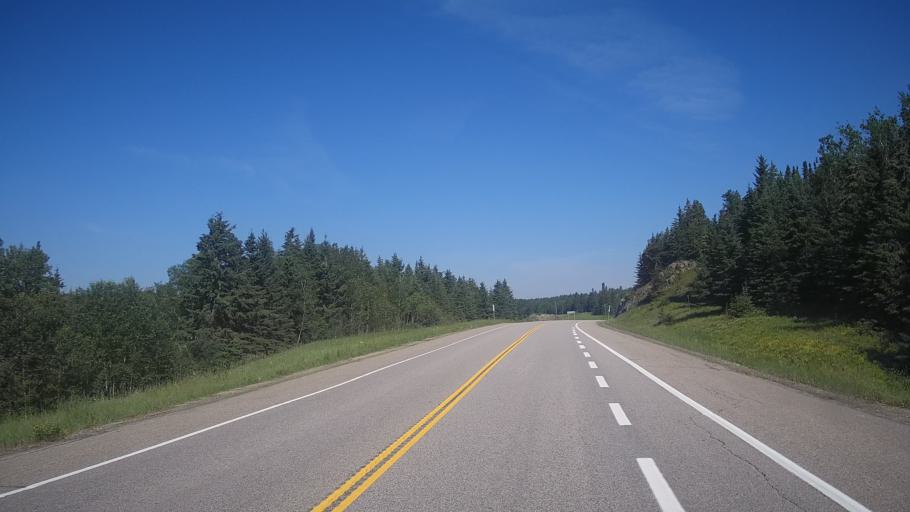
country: CA
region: Ontario
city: Dryden
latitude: 49.7530
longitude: -92.6469
